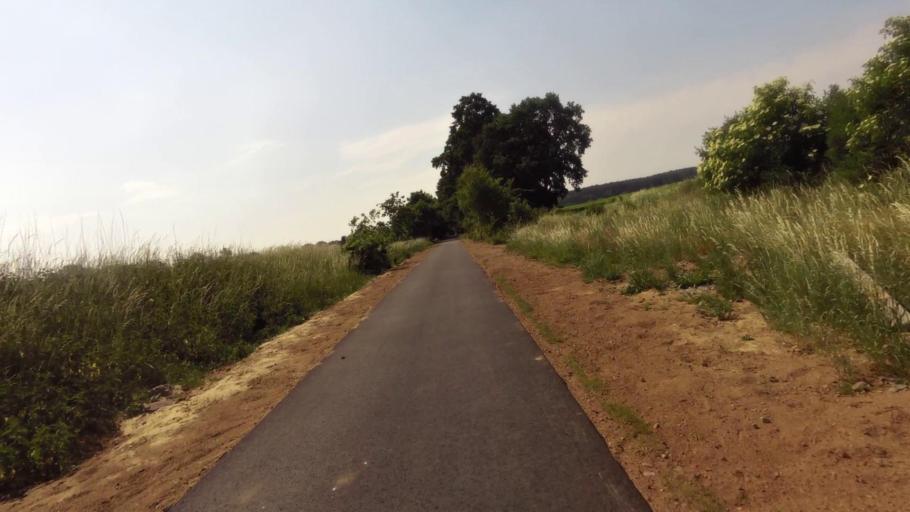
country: PL
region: West Pomeranian Voivodeship
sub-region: Powiat gryfinski
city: Gryfino
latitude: 53.2221
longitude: 14.5624
